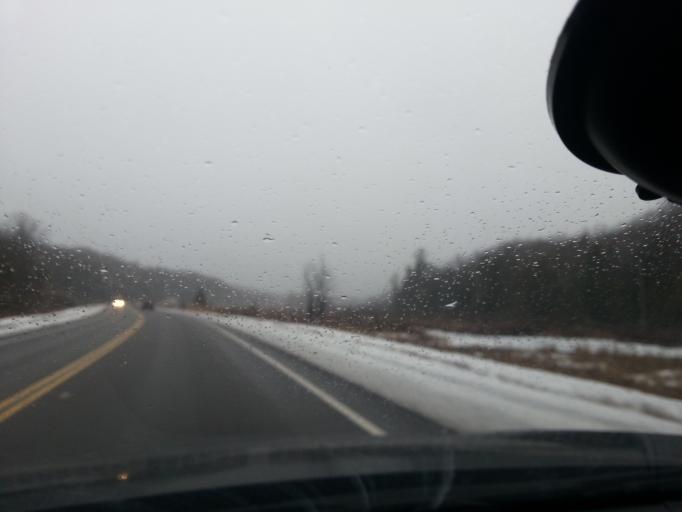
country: CA
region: Ontario
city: Perth
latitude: 44.7697
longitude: -76.7435
